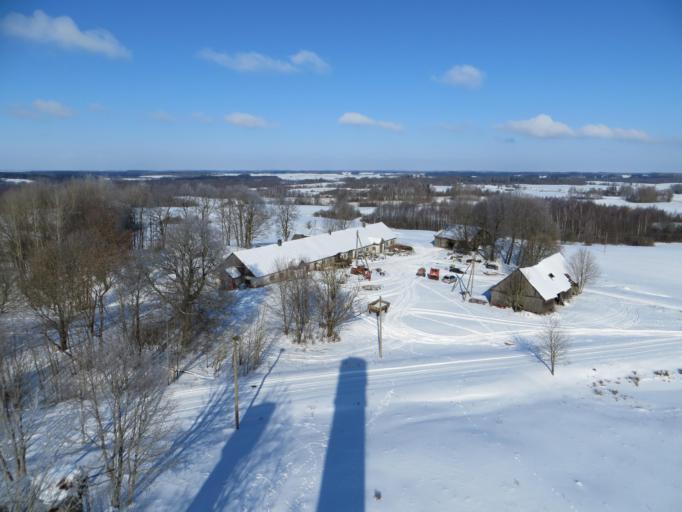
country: LT
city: Zarasai
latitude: 55.7730
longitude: 25.9951
